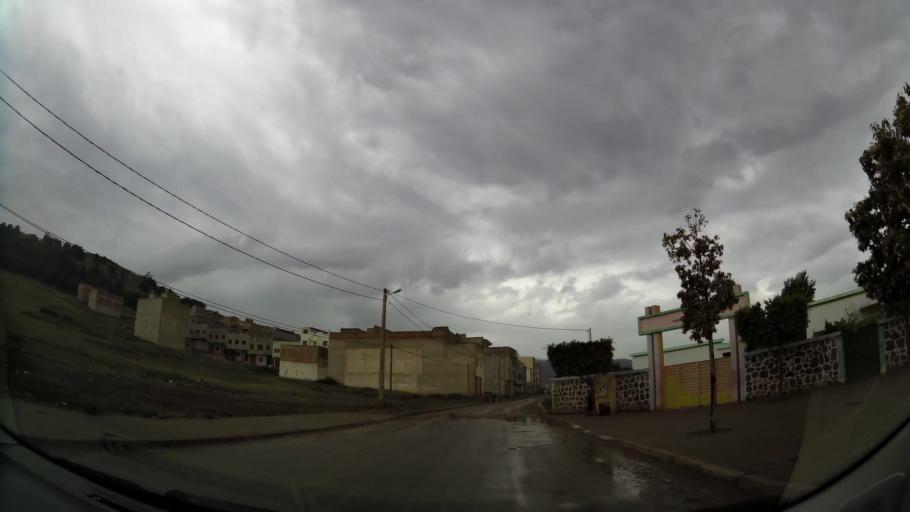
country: MA
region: Oriental
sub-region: Nador
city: Nador
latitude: 35.1468
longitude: -2.9783
